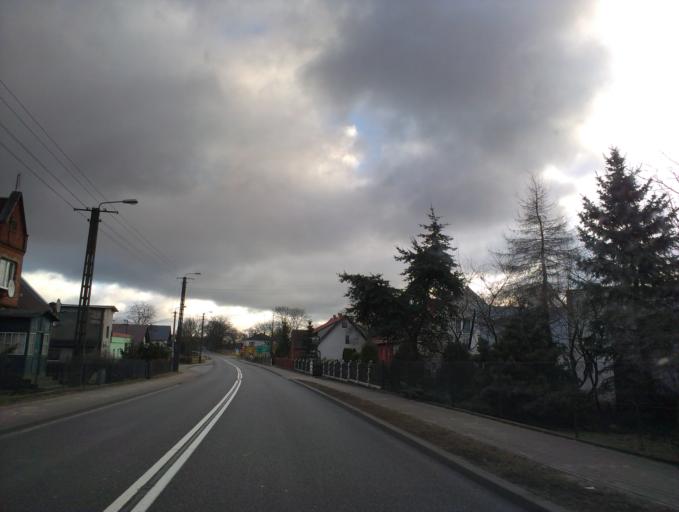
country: PL
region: Pomeranian Voivodeship
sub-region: Powiat czluchowski
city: Debrzno
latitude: 53.6255
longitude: 17.2284
